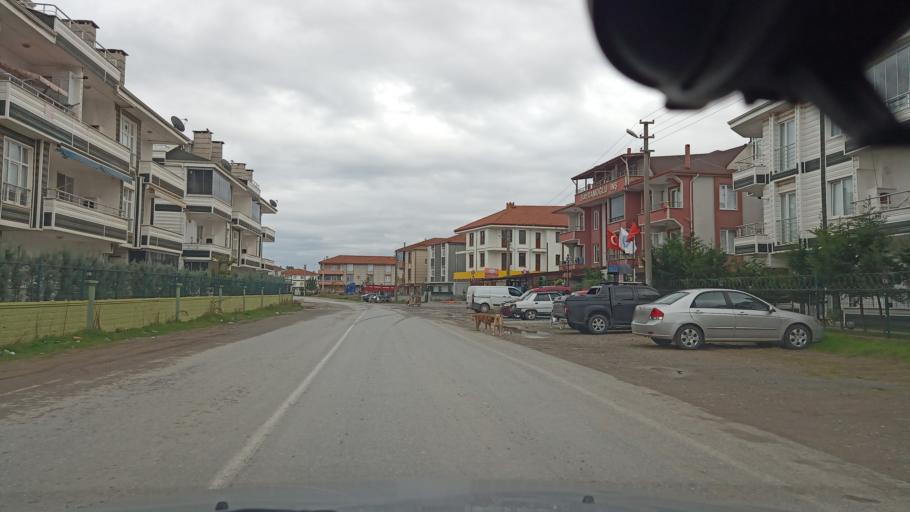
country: TR
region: Sakarya
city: Karasu
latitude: 41.1109
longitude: 30.6795
